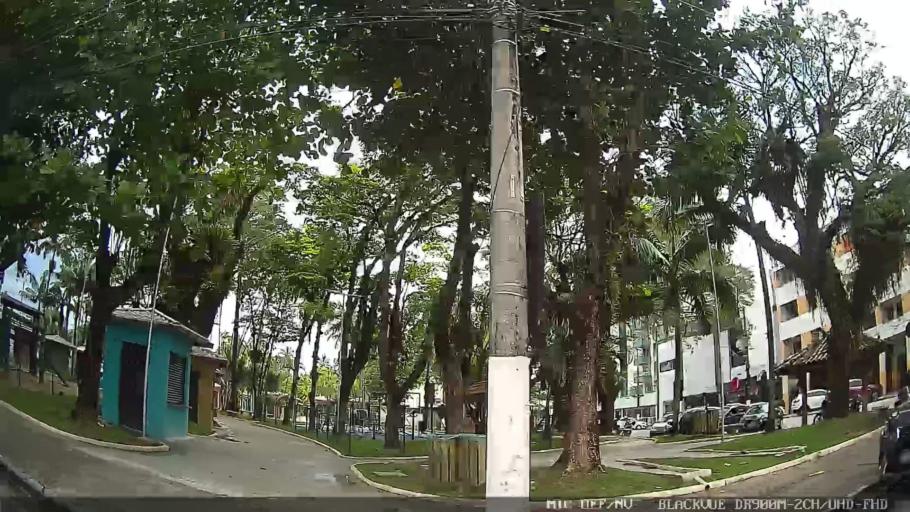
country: BR
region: Sao Paulo
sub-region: Caraguatatuba
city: Caraguatatuba
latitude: -23.6222
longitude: -45.4072
